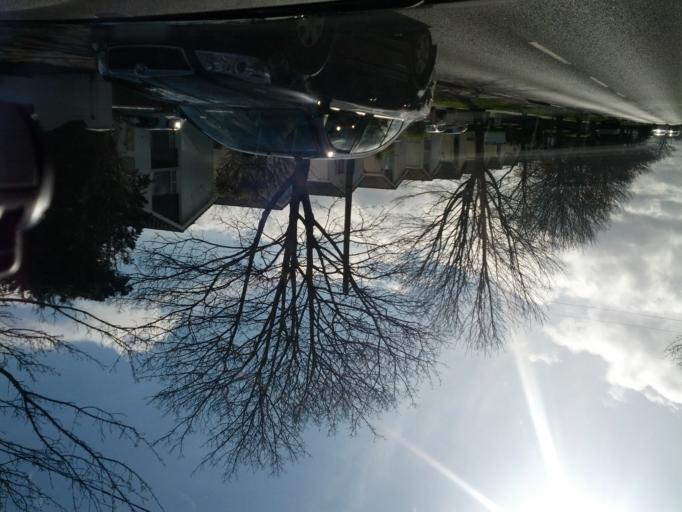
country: IE
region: Leinster
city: Portmarnock
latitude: 53.4249
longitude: -6.1322
